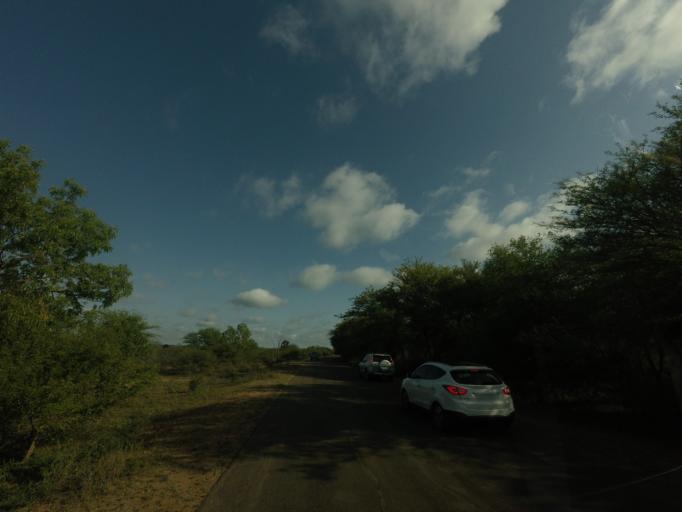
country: ZA
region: Mpumalanga
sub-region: Ehlanzeni District
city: Komatipoort
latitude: -25.2556
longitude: 31.8467
